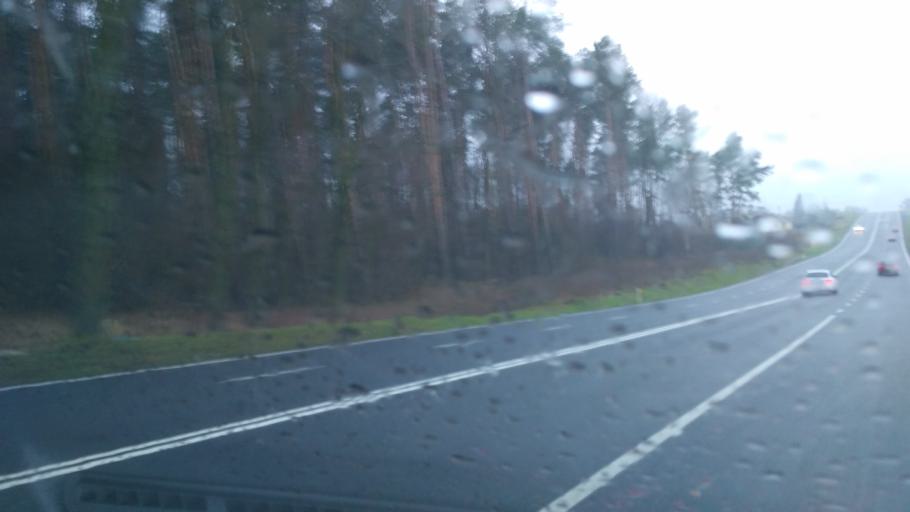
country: PL
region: Subcarpathian Voivodeship
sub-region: Powiat przeworski
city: Nowosielce
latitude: 50.0648
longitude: 22.4225
